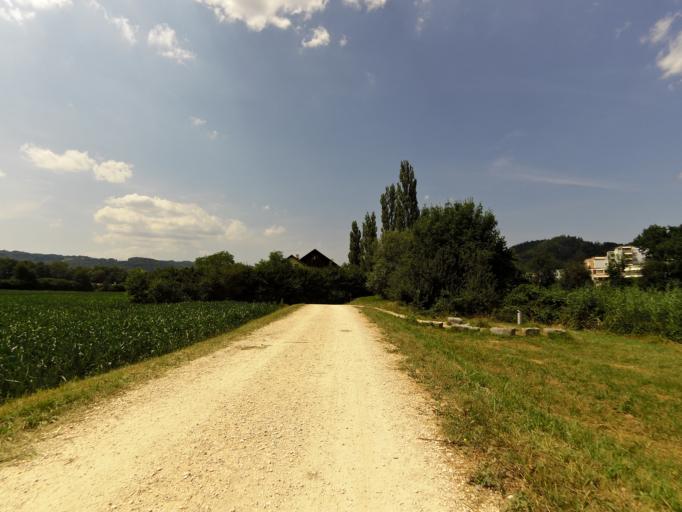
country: CH
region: Zurich
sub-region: Bezirk Dietikon
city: Geroldswil
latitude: 47.4258
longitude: 8.3940
